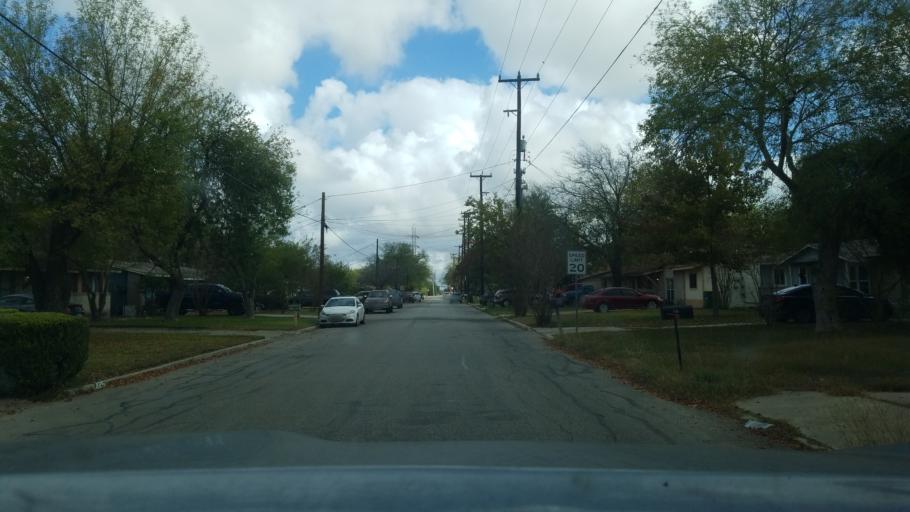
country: US
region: Texas
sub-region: Bexar County
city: Universal City
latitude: 29.5426
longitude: -98.2933
